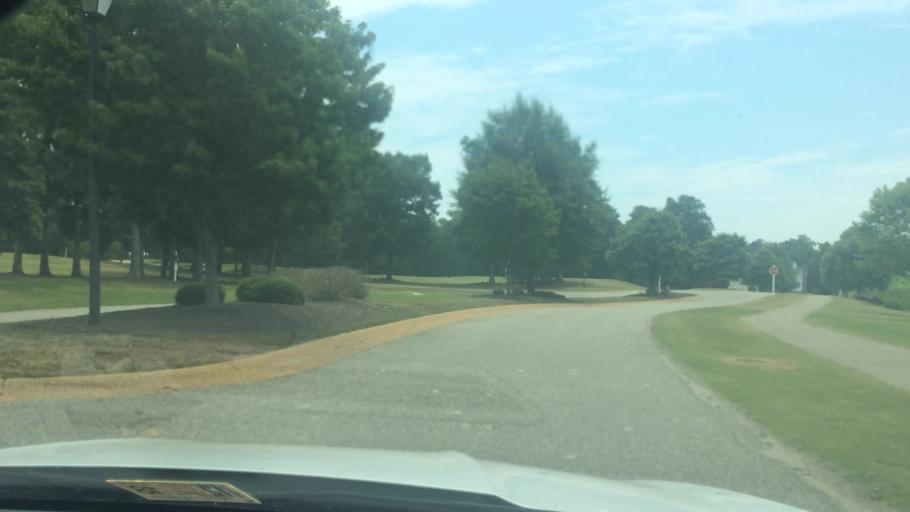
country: US
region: Virginia
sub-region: James City County
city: Williamsburg
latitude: 37.2719
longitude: -76.8120
